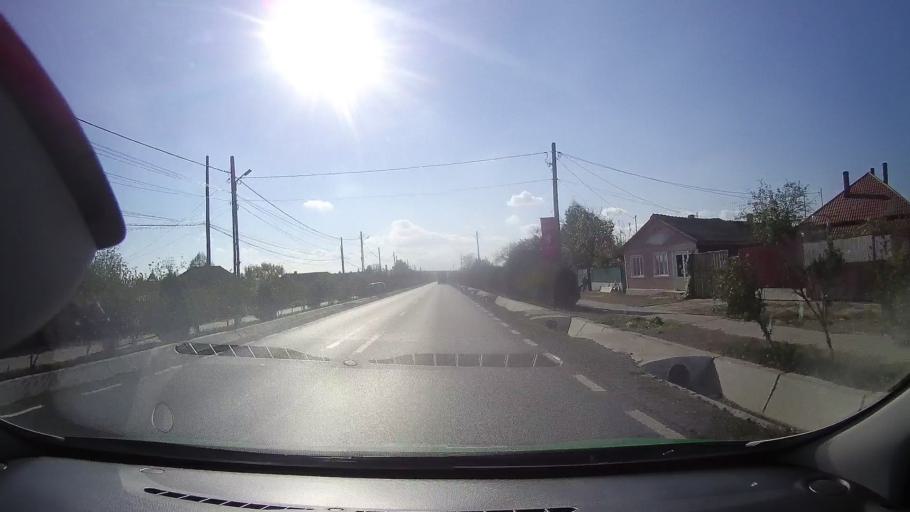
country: RO
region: Tulcea
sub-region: Comuna Baia
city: Baia
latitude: 44.7314
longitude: 28.6817
